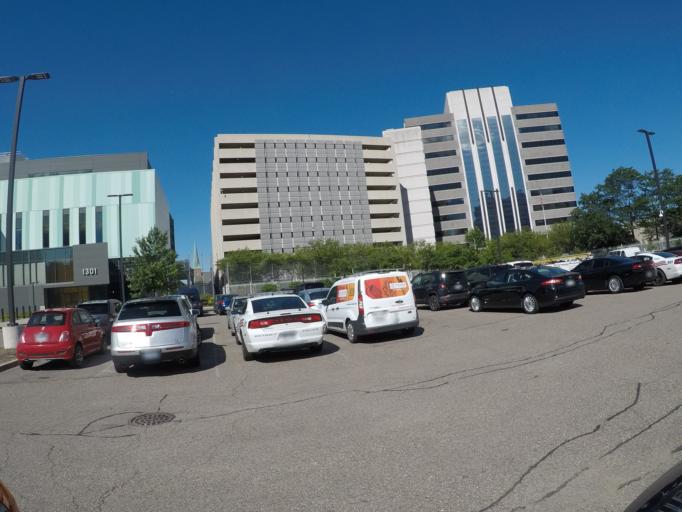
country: US
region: Michigan
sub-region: Wayne County
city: Detroit
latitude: 42.3310
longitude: -83.0575
